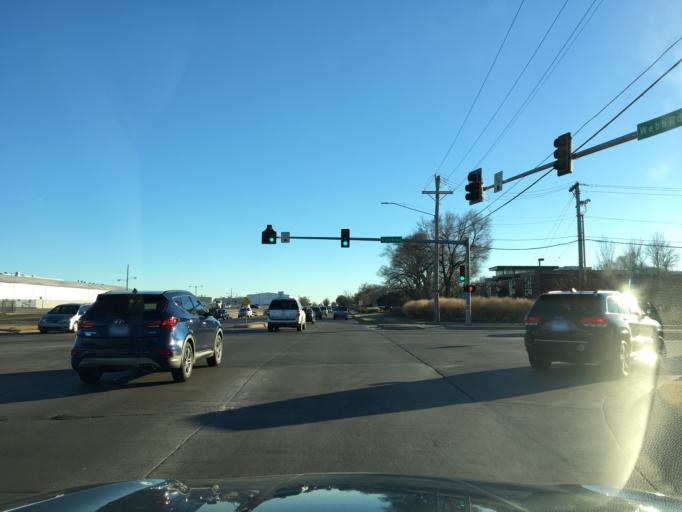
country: US
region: Kansas
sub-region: Sedgwick County
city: Bellaire
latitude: 37.6943
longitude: -97.2263
